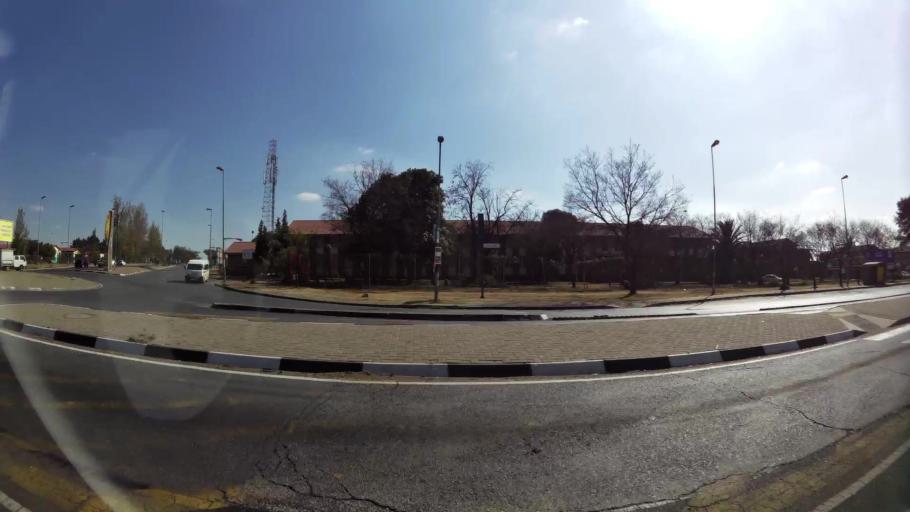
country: ZA
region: Gauteng
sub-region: City of Johannesburg Metropolitan Municipality
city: Soweto
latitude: -26.2688
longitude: 27.8761
